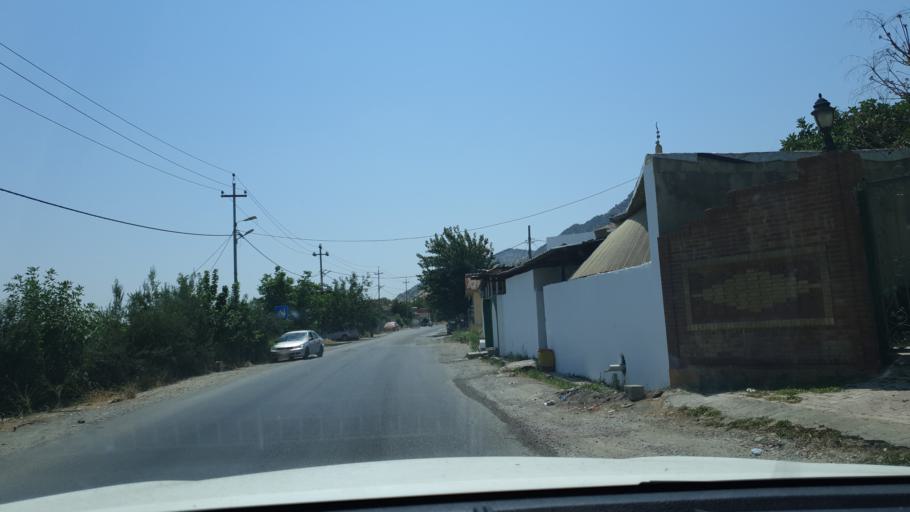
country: IQ
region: Arbil
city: Nahiyat Hiran
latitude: 36.2961
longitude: 44.4740
